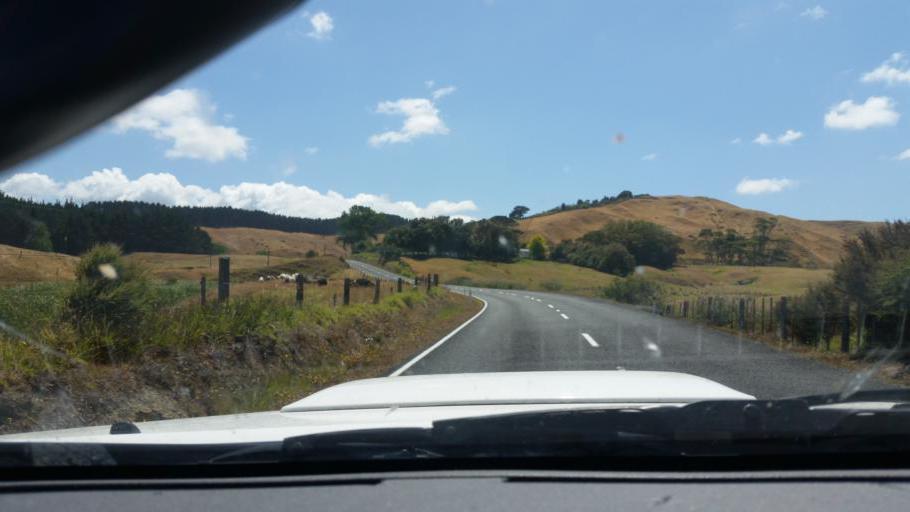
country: NZ
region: Northland
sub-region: Kaipara District
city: Dargaville
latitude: -35.8250
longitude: 173.6780
